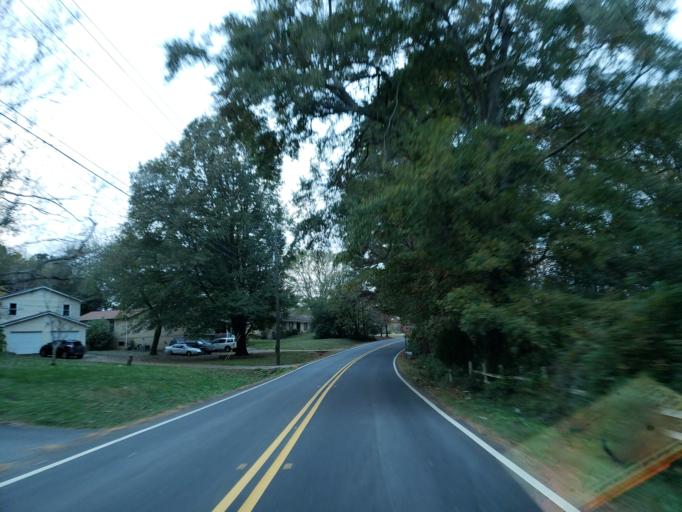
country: US
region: Georgia
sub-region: Cobb County
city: Acworth
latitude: 34.0191
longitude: -84.6821
